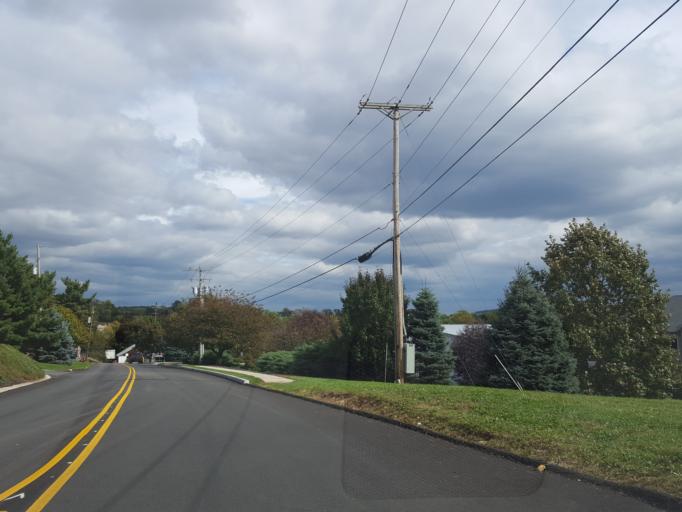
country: US
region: Pennsylvania
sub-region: York County
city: Spry
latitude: 39.9116
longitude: -76.6811
